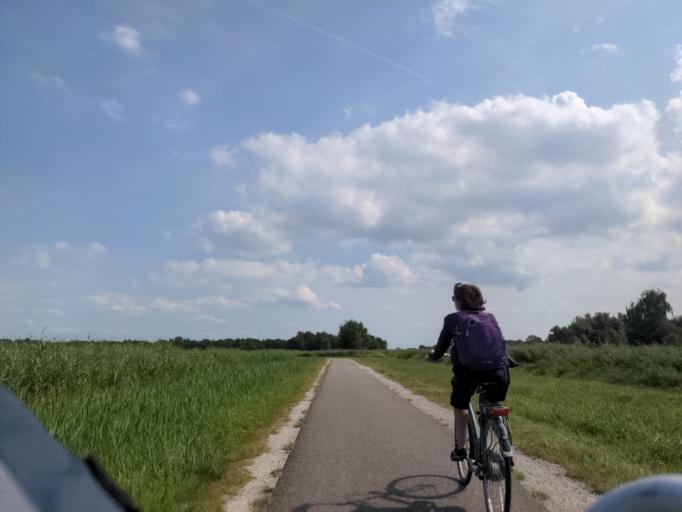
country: NL
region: North Holland
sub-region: Gemeente Landsmeer
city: Landsmeer
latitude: 52.4450
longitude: 4.8947
